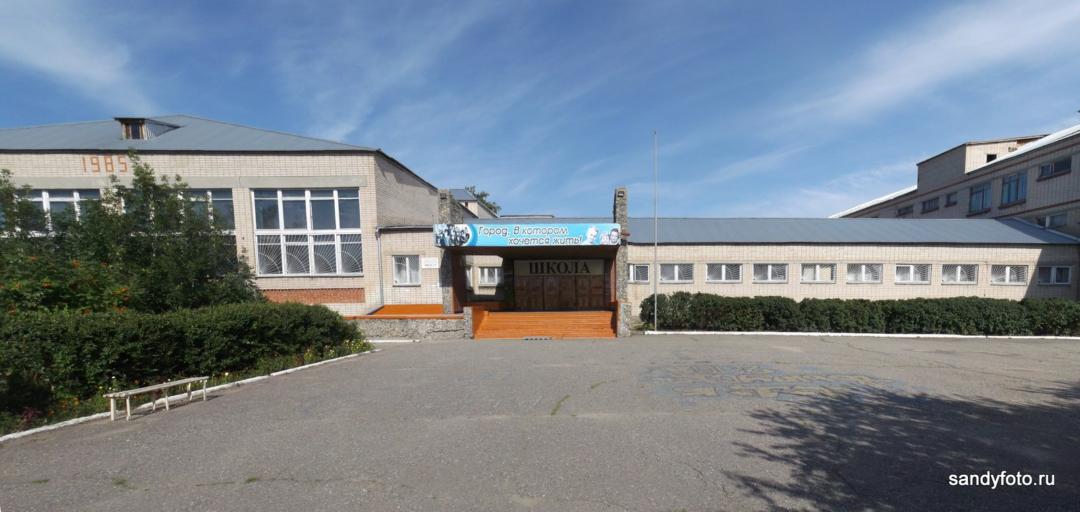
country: RU
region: Chelyabinsk
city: Troitsk
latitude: 54.0818
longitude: 61.5516
